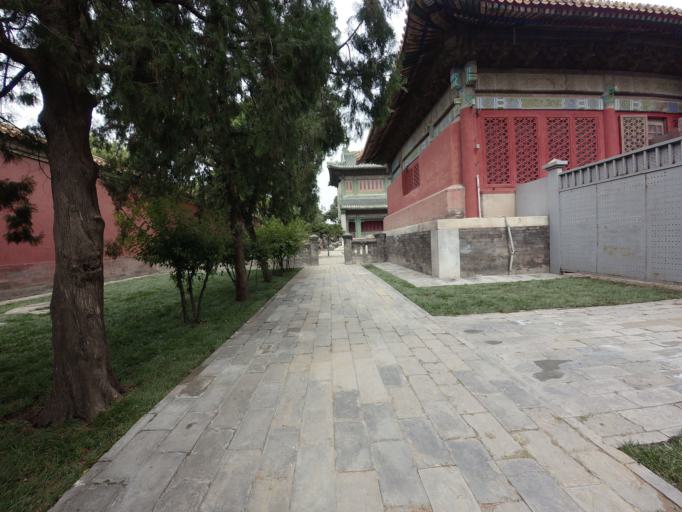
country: CN
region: Beijing
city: Beijing
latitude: 39.9142
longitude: 116.3929
